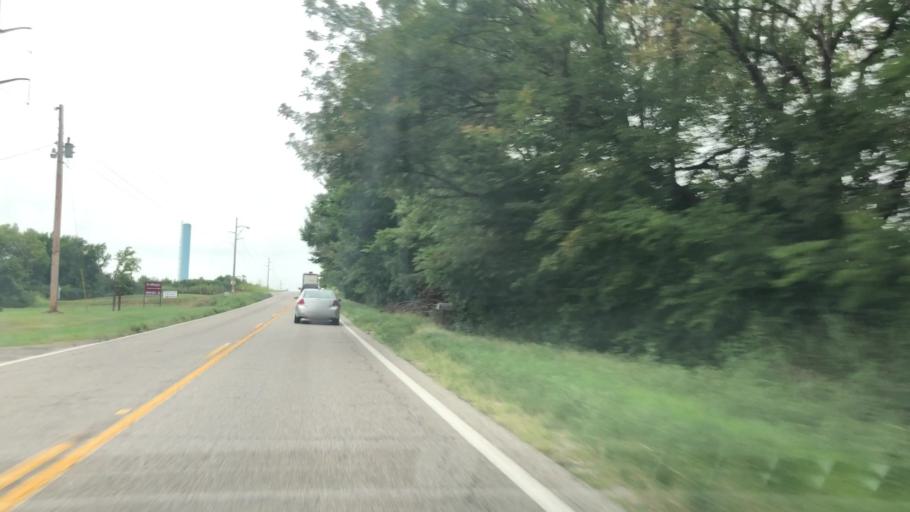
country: US
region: Oklahoma
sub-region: Washington County
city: Dewey
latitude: 36.7280
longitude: -95.8531
